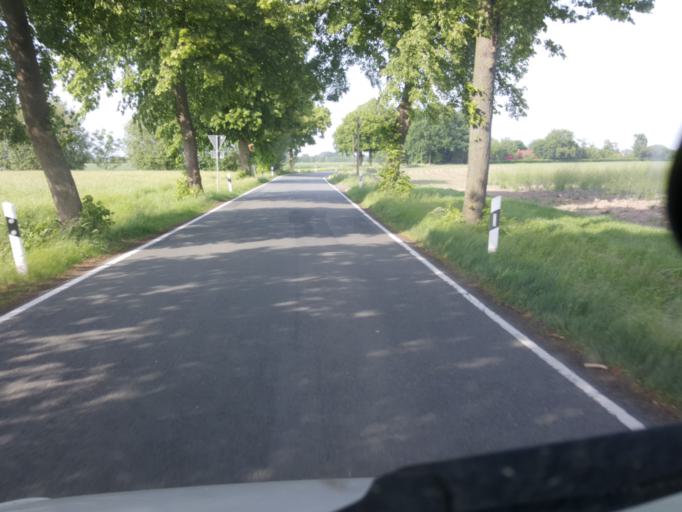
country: DE
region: North Rhine-Westphalia
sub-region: Regierungsbezirk Detmold
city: Minden
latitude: 52.3386
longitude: 8.8436
